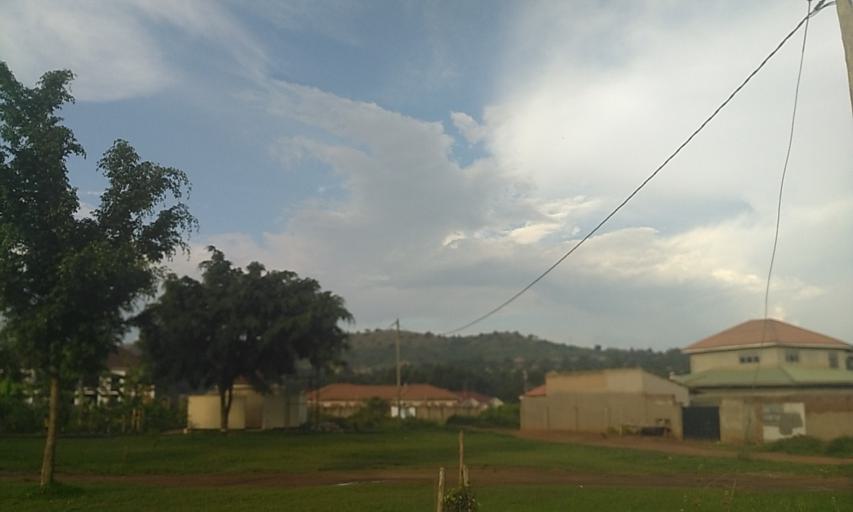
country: UG
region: Central Region
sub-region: Wakiso District
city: Kajansi
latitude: 0.2692
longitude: 32.5256
